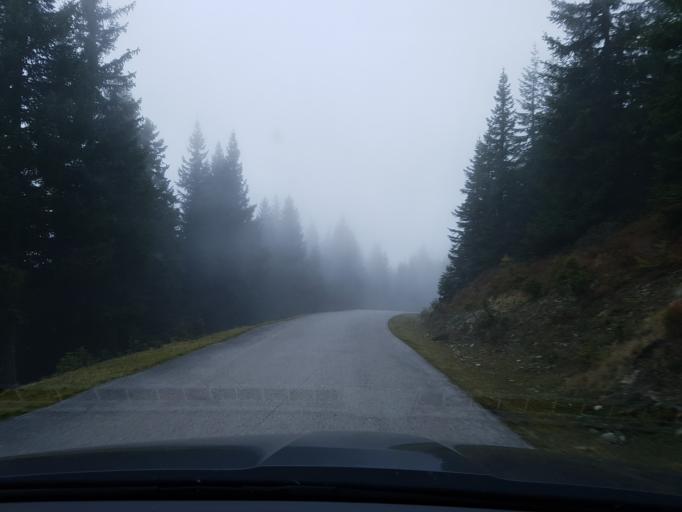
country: AT
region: Salzburg
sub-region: Politischer Bezirk Sankt Johann im Pongau
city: Filzmoos
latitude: 47.4116
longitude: 13.4863
